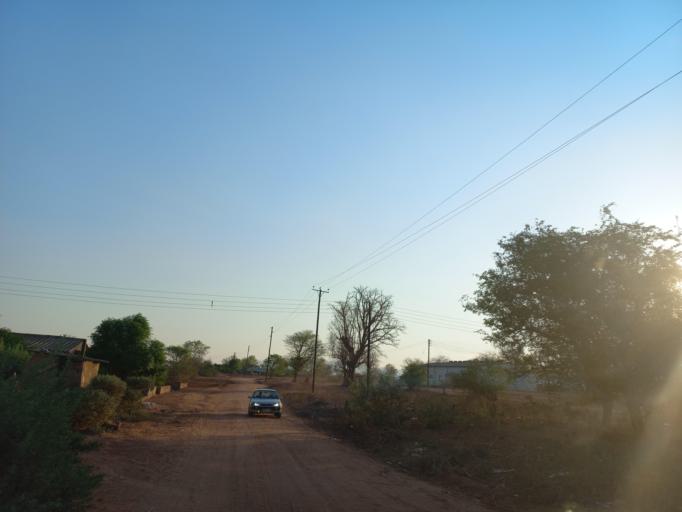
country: ZM
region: Lusaka
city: Luangwa
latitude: -15.6145
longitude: 30.3913
